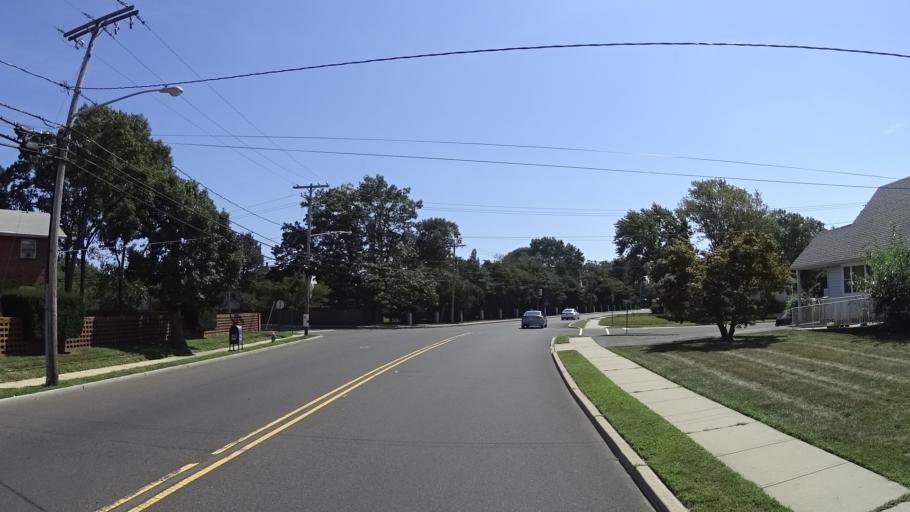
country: US
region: New Jersey
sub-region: Monmouth County
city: Shark River Hills
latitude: 40.2047
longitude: -74.0431
